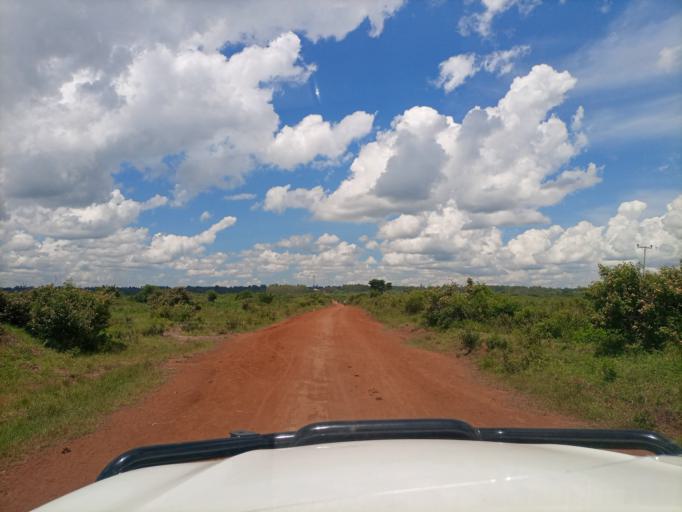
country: UG
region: Eastern Region
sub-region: Busia District
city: Busia
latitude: 0.6271
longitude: 33.9902
